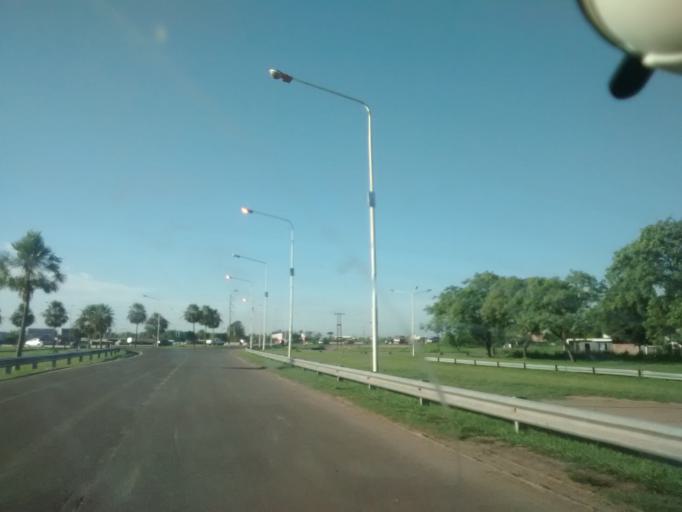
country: AR
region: Chaco
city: Fontana
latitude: -27.4449
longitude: -59.0246
